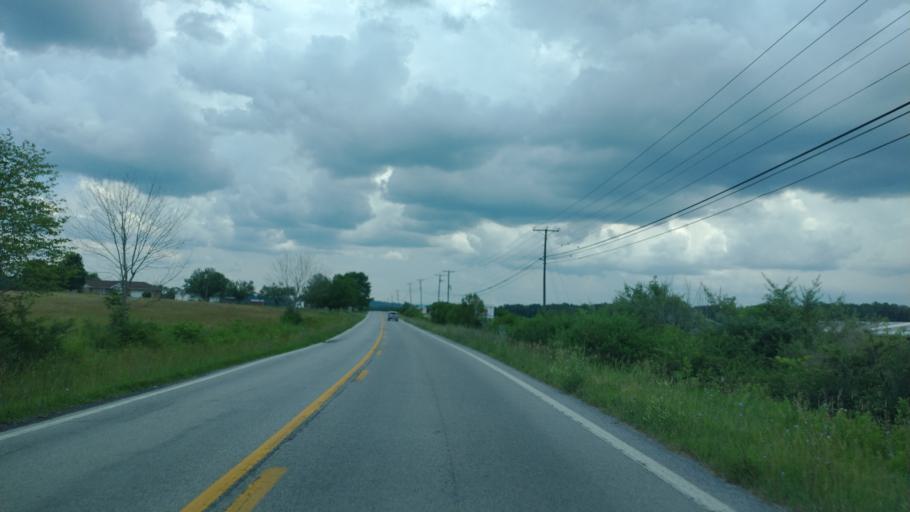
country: US
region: West Virginia
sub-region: Mercer County
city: Athens
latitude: 37.4543
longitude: -81.0093
